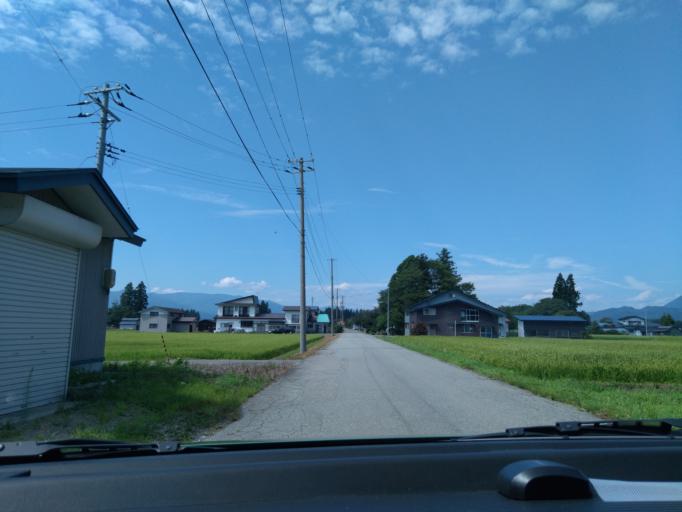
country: JP
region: Akita
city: Kakunodatemachi
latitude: 39.6061
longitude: 140.5957
